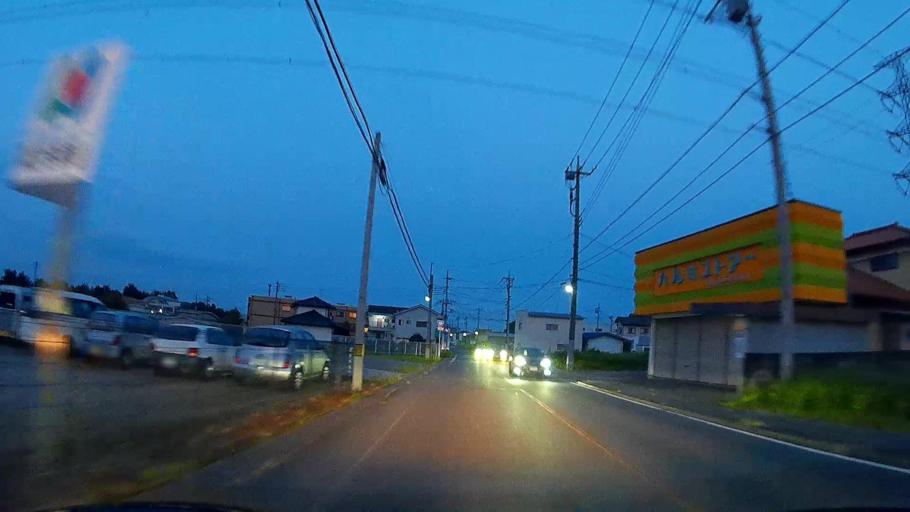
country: JP
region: Gunma
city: Takasaki
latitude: 36.3427
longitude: 138.9670
